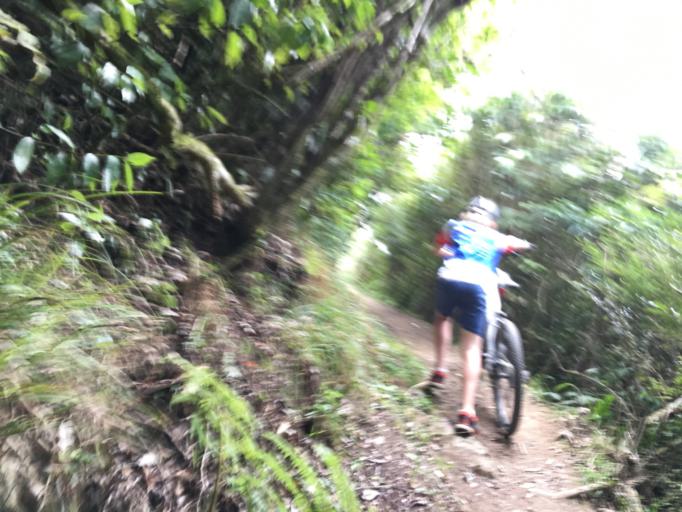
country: NZ
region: Wellington
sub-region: Wellington City
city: Brooklyn
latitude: -41.2957
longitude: 174.7413
